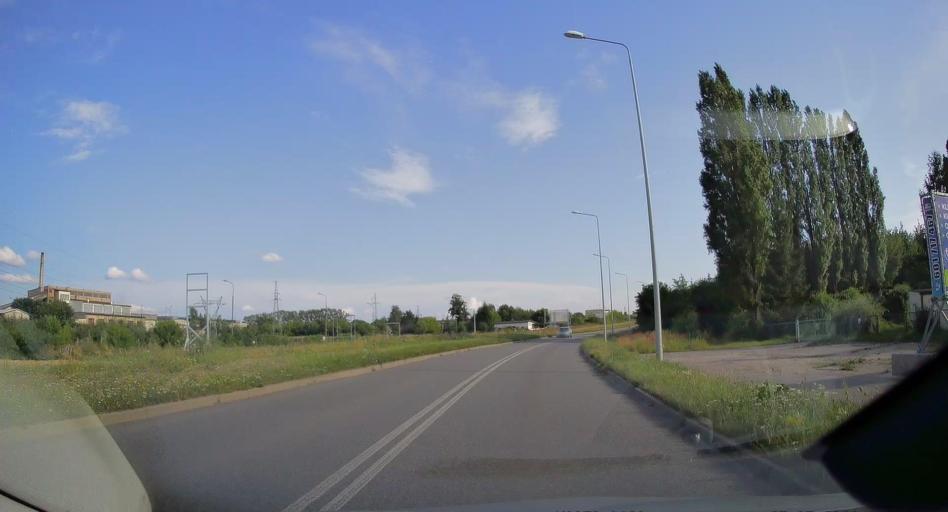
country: PL
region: Swietokrzyskie
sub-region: Powiat konecki
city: Konskie
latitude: 51.2037
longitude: 20.4002
